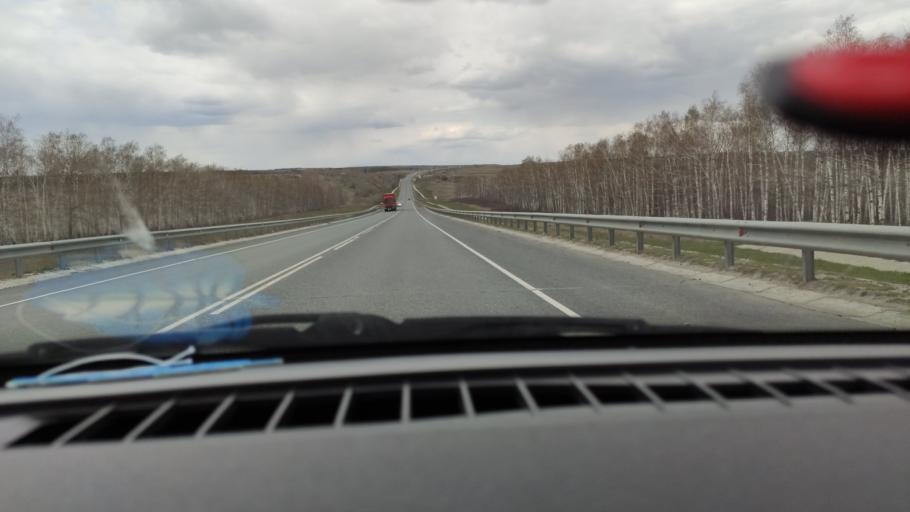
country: RU
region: Saratov
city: Shikhany
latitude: 52.1256
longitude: 47.2445
